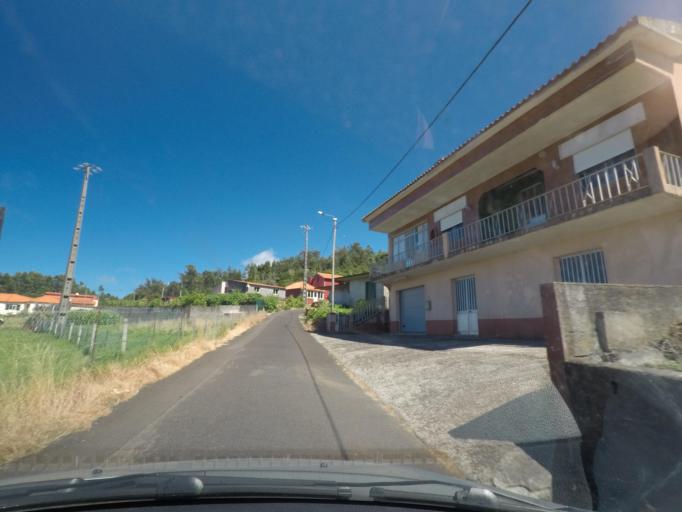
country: PT
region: Madeira
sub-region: Porto Moniz
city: Porto Moniz
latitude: 32.8418
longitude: -17.2060
